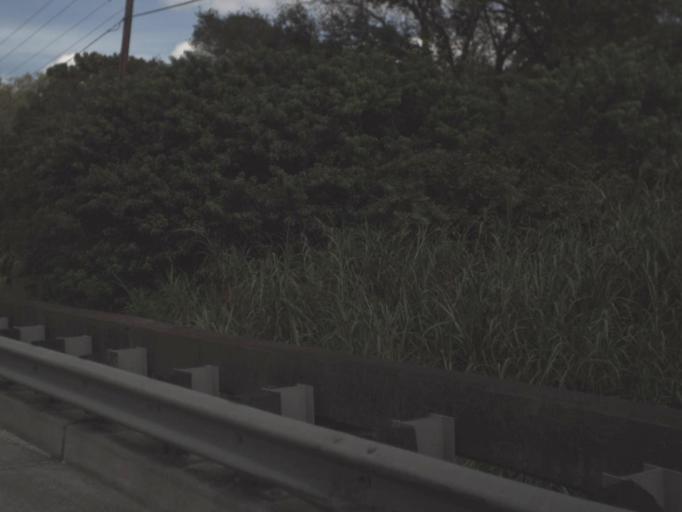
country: US
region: Florida
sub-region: Okeechobee County
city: Cypress Quarters
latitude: 27.2963
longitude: -80.8274
